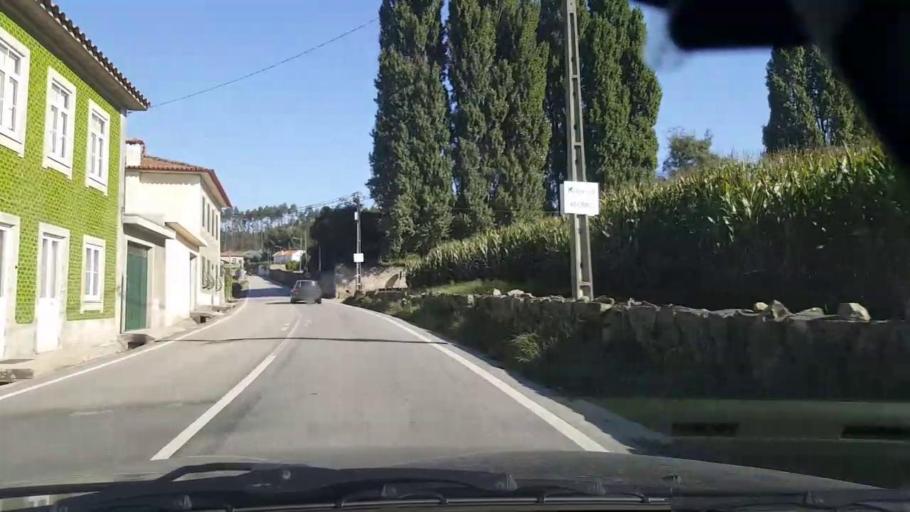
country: PT
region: Porto
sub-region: Maia
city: Gemunde
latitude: 41.3263
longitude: -8.6556
